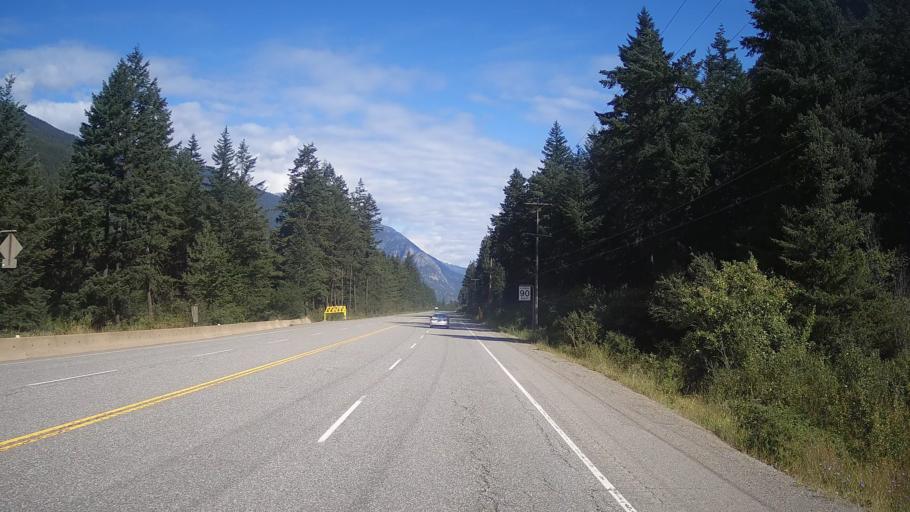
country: CA
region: British Columbia
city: Hope
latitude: 50.0381
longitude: -121.5342
